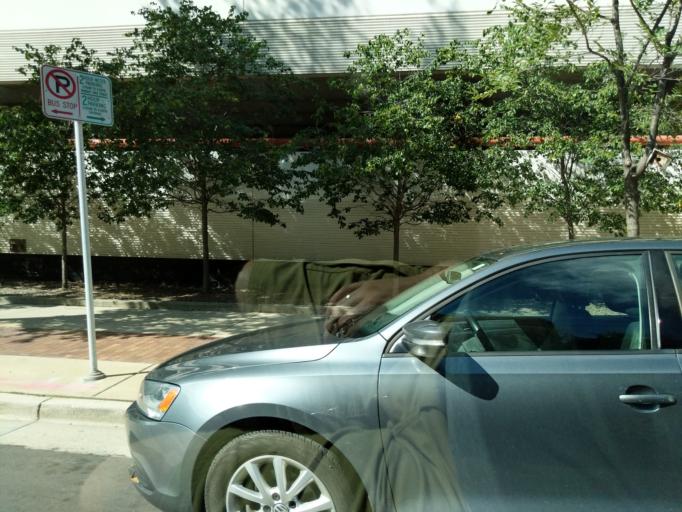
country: US
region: Wisconsin
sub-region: Milwaukee County
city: Milwaukee
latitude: 43.0416
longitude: -87.9069
